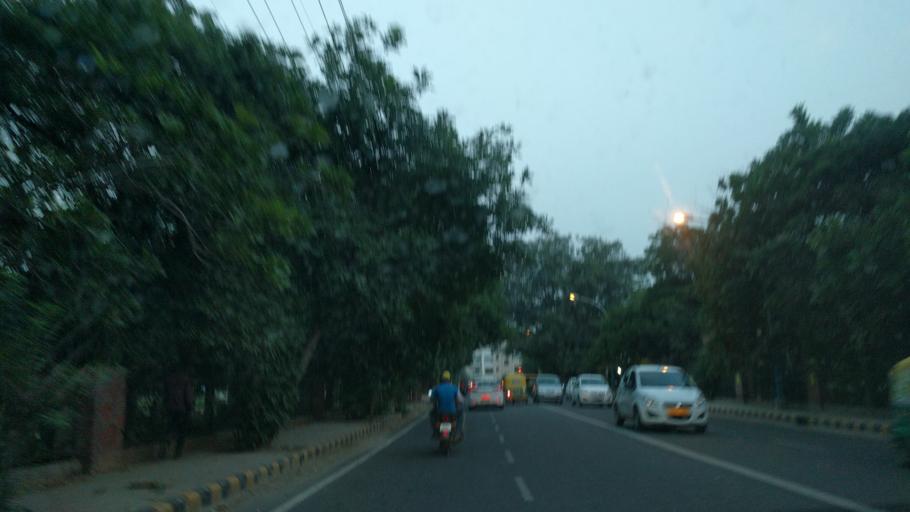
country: IN
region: Haryana
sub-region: Gurgaon
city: Gurgaon
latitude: 28.4507
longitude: 77.0628
